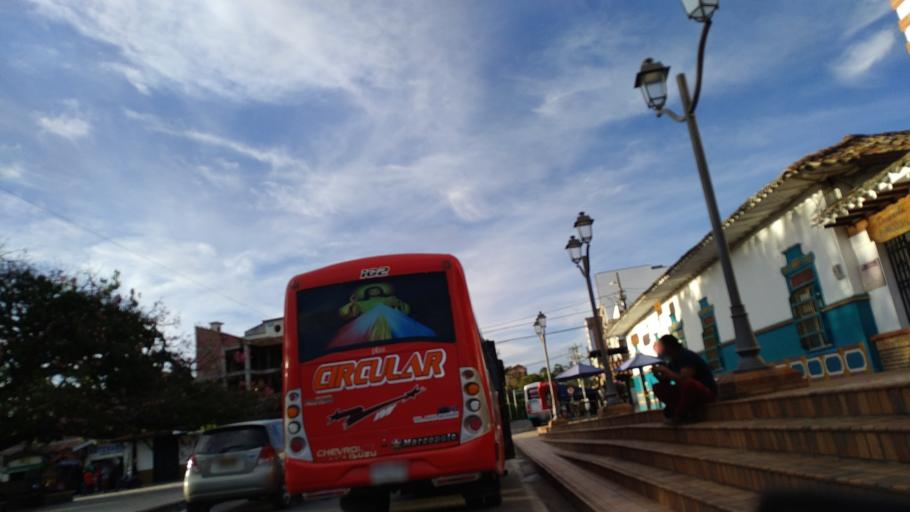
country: CO
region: Antioquia
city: Rionegro
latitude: 6.1302
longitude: -75.3797
